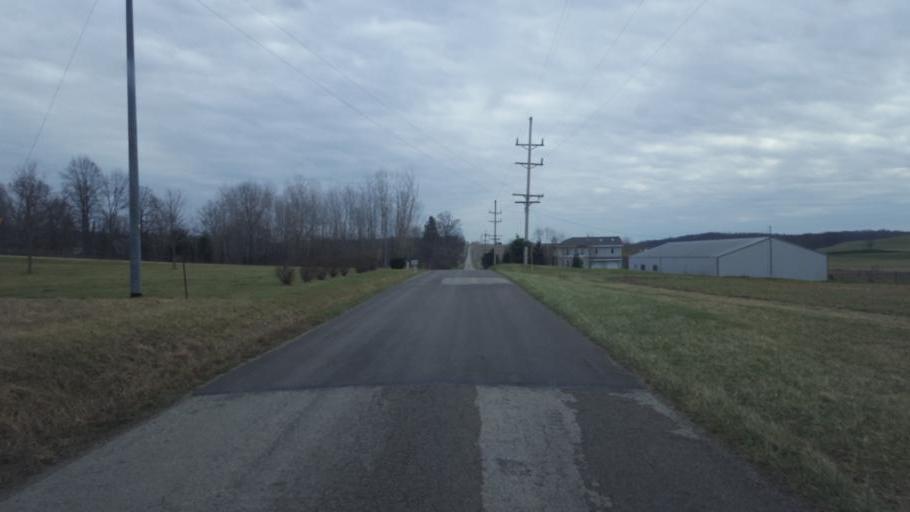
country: US
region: Ohio
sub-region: Knox County
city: Fredericktown
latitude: 40.5245
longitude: -82.4811
